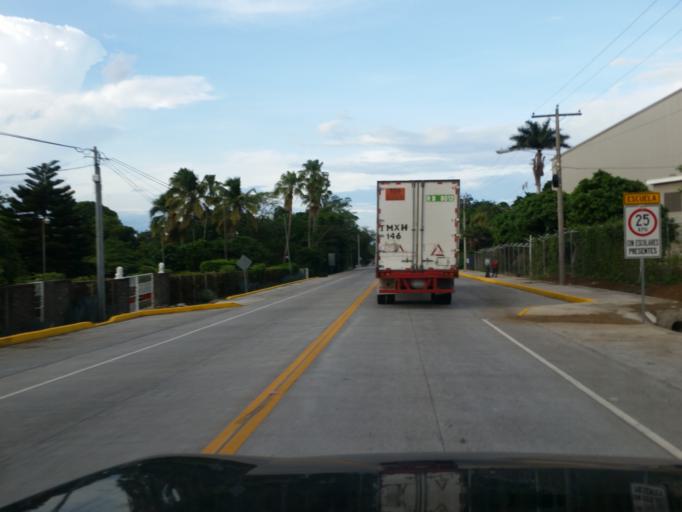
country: NI
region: Managua
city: Ciudad Sandino
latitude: 12.0889
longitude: -86.3566
